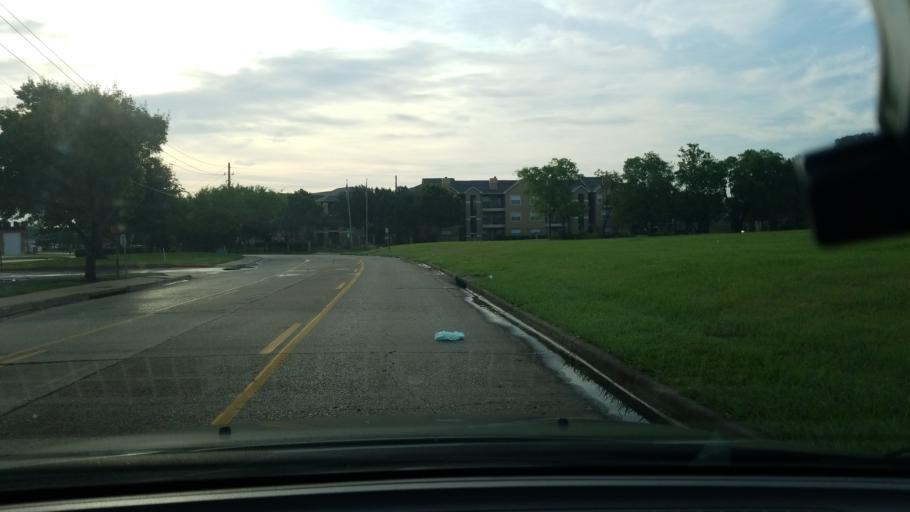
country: US
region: Texas
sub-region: Dallas County
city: Mesquite
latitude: 32.8067
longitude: -96.6167
